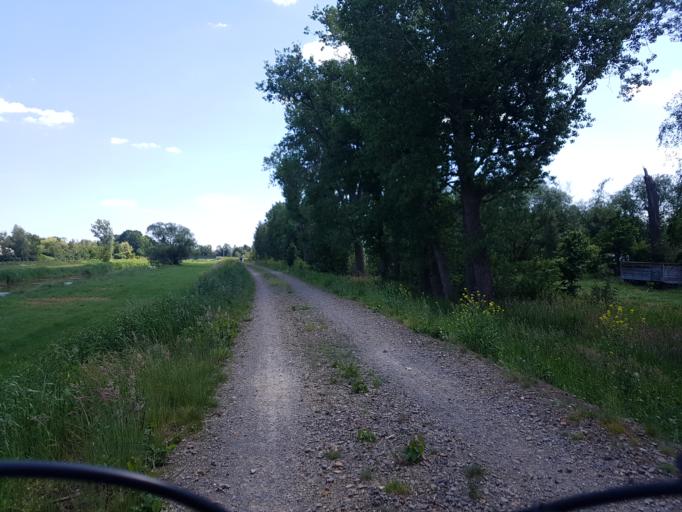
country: DE
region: Brandenburg
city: Bad Liebenwerda
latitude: 51.5247
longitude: 13.3850
